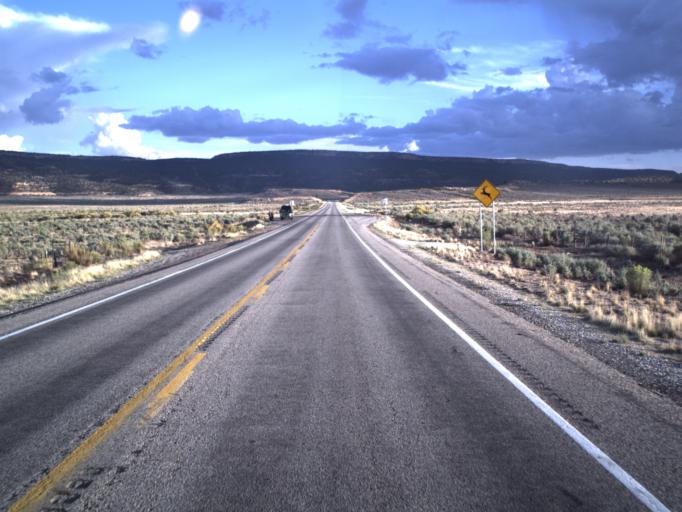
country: US
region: Utah
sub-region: San Juan County
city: Monticello
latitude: 38.0700
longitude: -109.3486
